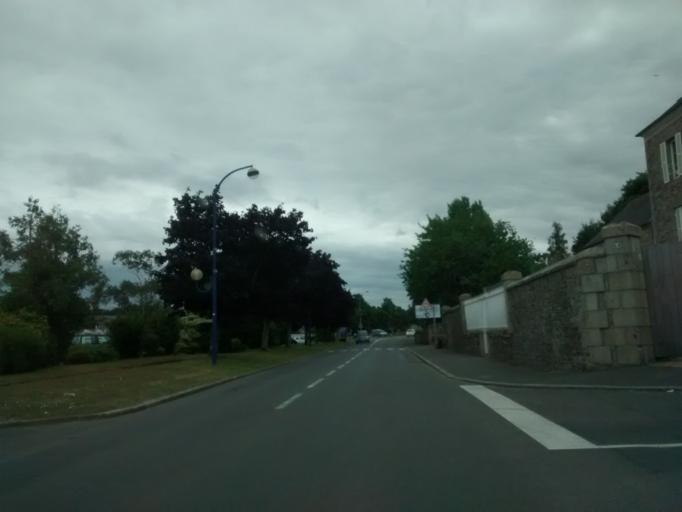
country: FR
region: Brittany
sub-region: Departement des Cotes-d'Armor
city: Minihy-Treguier
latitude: 48.7860
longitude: -3.2232
